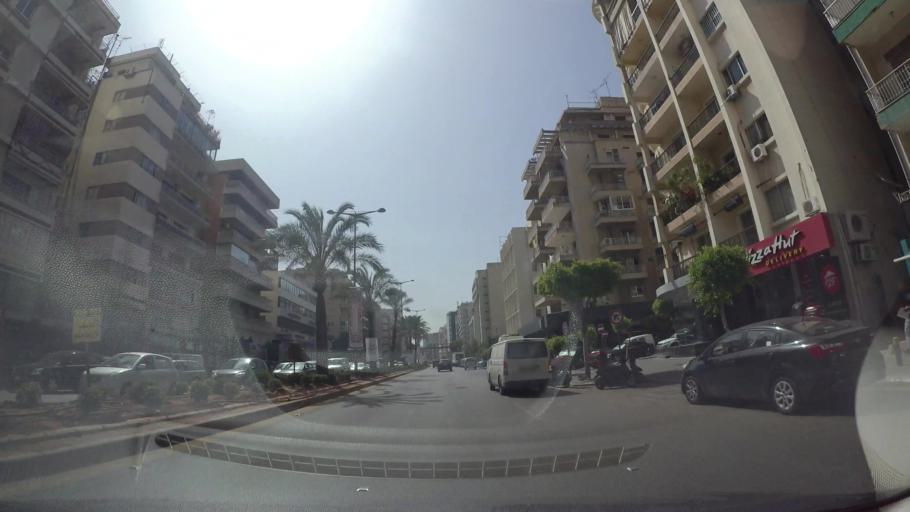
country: LB
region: Beyrouth
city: Beirut
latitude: 33.8803
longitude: 35.4929
